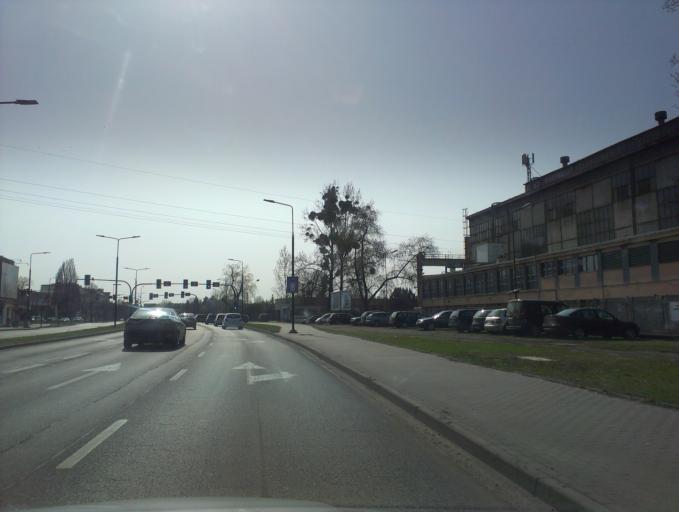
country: PL
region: Kujawsko-Pomorskie
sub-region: Bydgoszcz
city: Bydgoszcz
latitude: 53.1370
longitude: 18.0250
